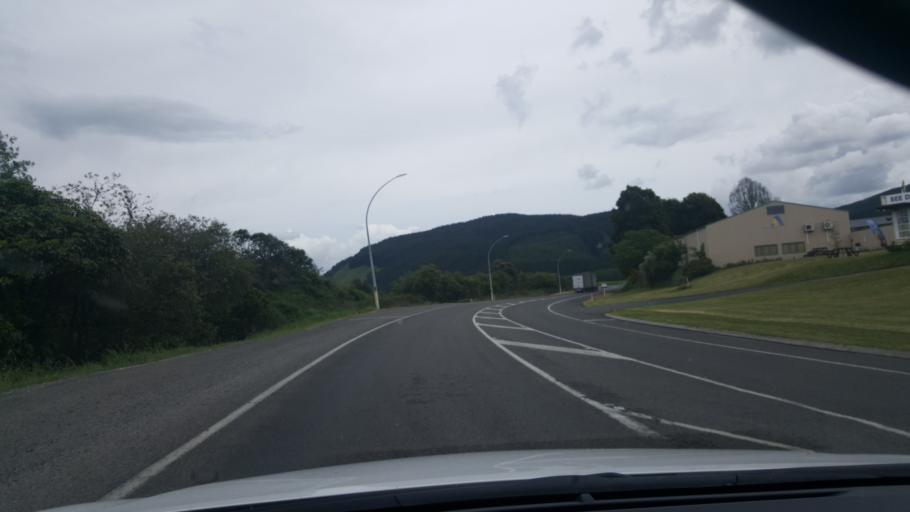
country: NZ
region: Bay of Plenty
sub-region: Rotorua District
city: Rotorua
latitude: -38.3408
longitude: 176.3636
